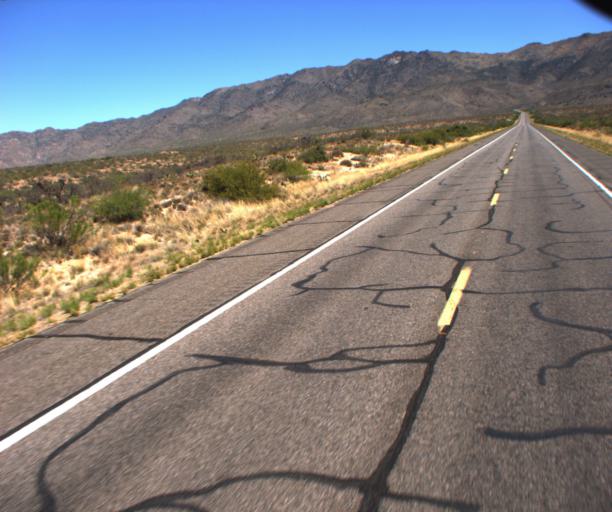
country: US
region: Arizona
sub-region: Yavapai County
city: Congress
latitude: 34.1868
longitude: -112.8215
